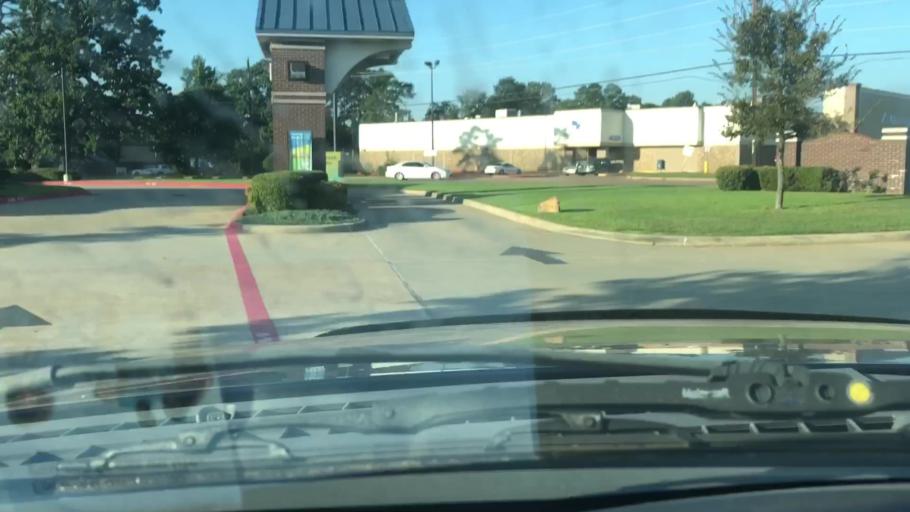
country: US
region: Texas
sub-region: Bowie County
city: Wake Village
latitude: 33.4537
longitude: -94.0841
